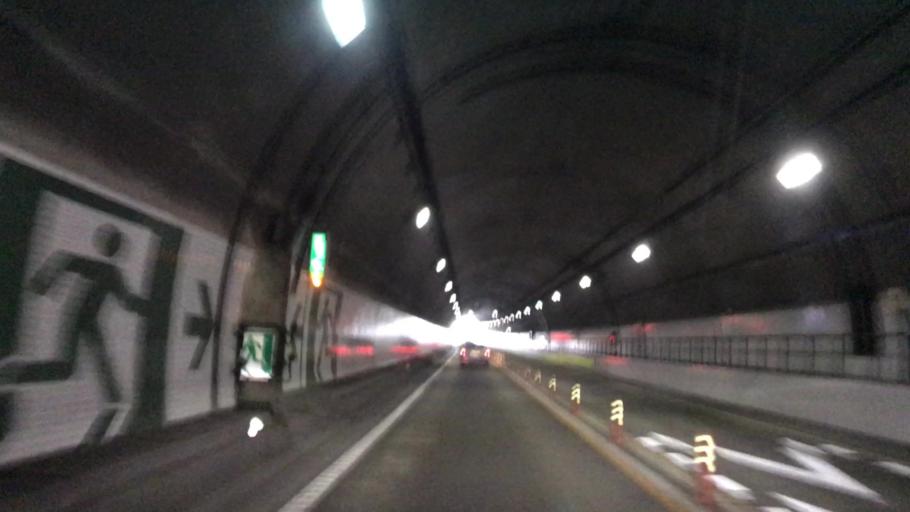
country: JP
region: Hokkaido
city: Shimo-furano
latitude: 42.9530
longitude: 142.3140
